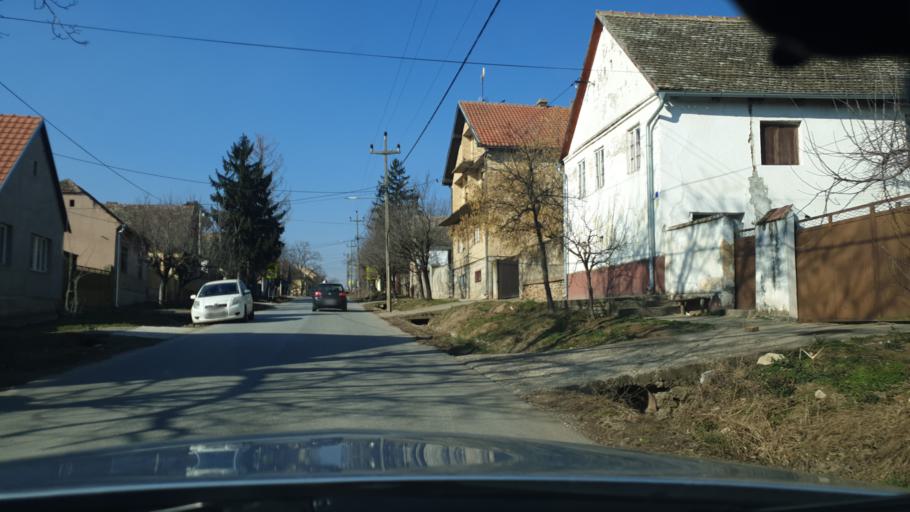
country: RS
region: Autonomna Pokrajina Vojvodina
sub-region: Sremski Okrug
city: Irig
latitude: 45.0875
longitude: 19.8361
